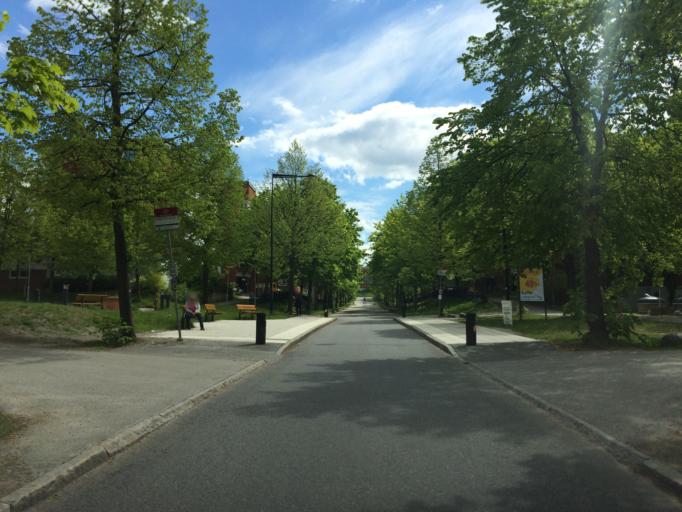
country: SE
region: Stockholm
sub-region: Botkyrka Kommun
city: Fittja
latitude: 59.2664
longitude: 17.8877
